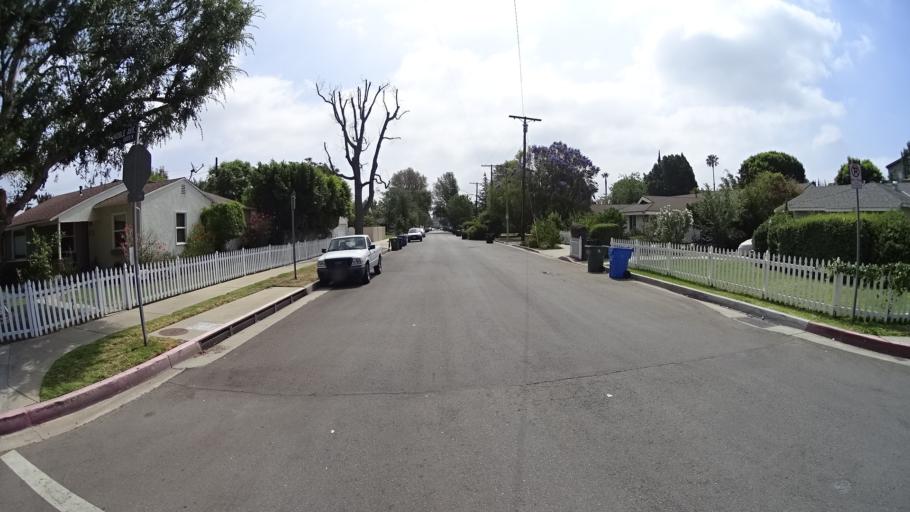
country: US
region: California
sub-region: Los Angeles County
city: Van Nuys
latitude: 34.1730
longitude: -118.4617
